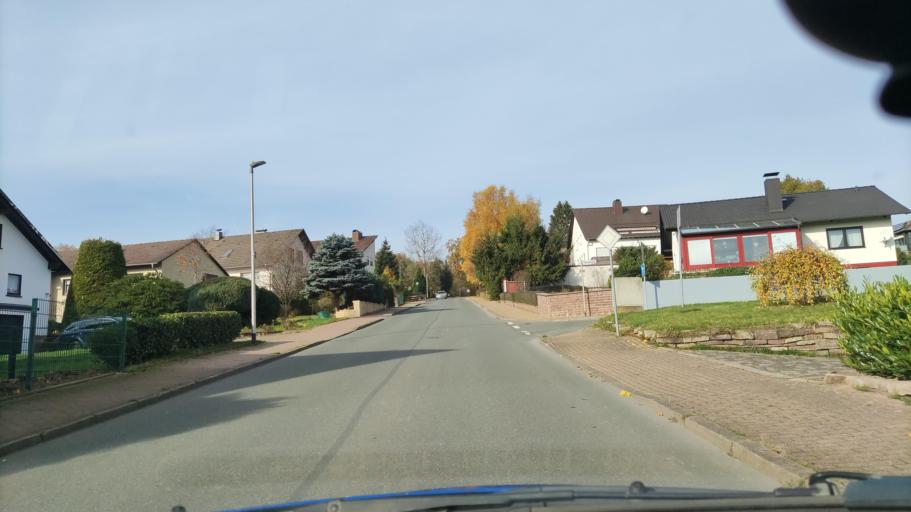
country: DE
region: Lower Saxony
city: Bevern
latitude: 51.7706
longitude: 9.5398
